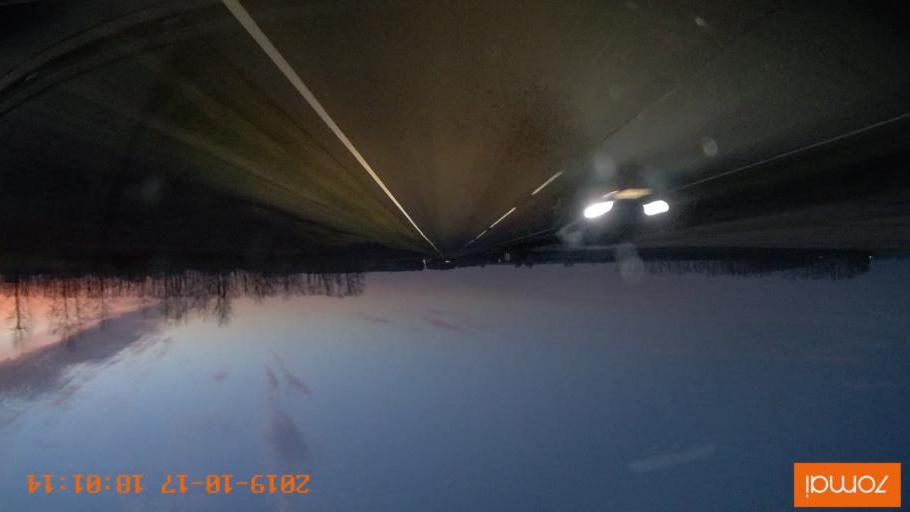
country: RU
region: Tula
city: Kurkino
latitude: 53.5102
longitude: 38.6109
